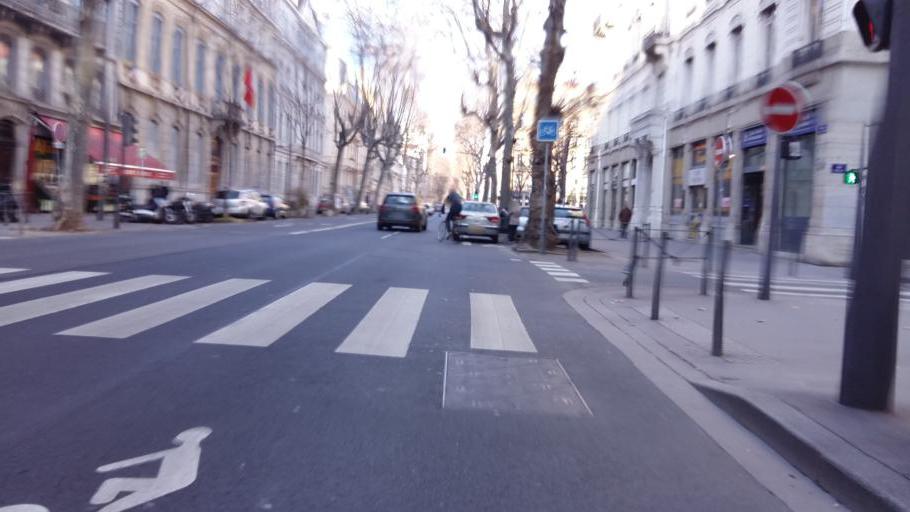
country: FR
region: Rhone-Alpes
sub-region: Departement du Rhone
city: Caluire-et-Cuire
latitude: 45.7704
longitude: 4.8436
